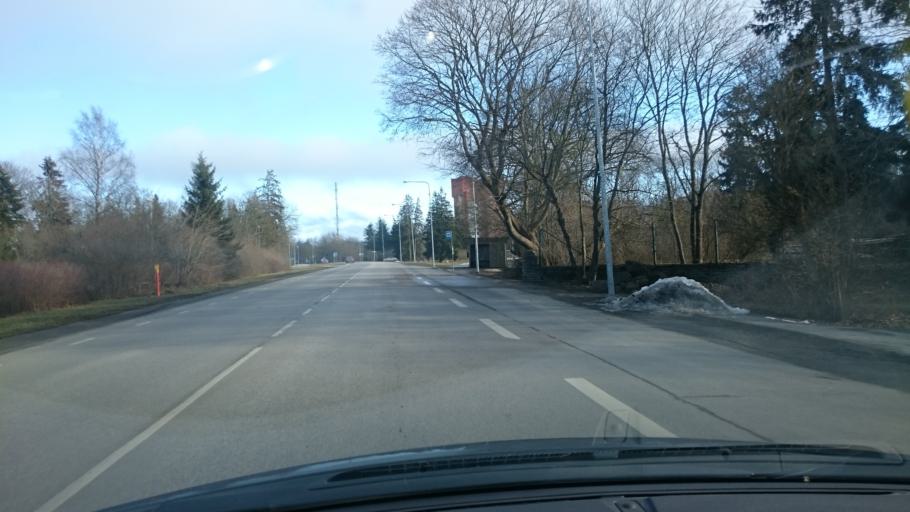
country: EE
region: Harju
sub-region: Harku vald
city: Tabasalu
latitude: 59.4305
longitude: 24.5382
